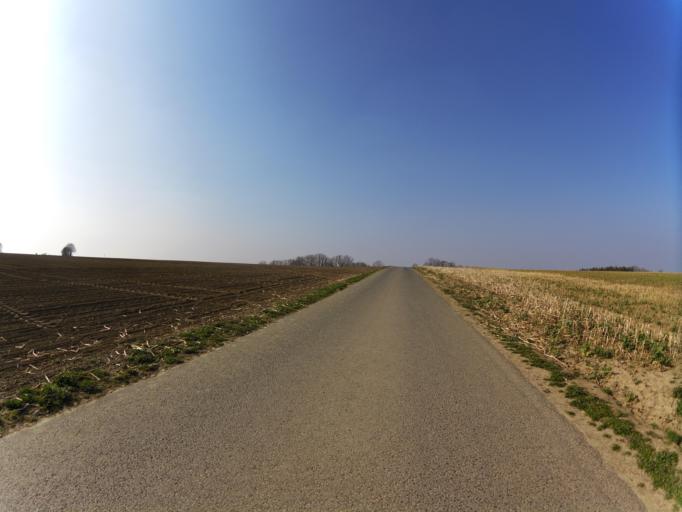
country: DE
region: Bavaria
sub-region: Regierungsbezirk Unterfranken
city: Gaukonigshofen
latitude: 49.6615
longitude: 9.9927
